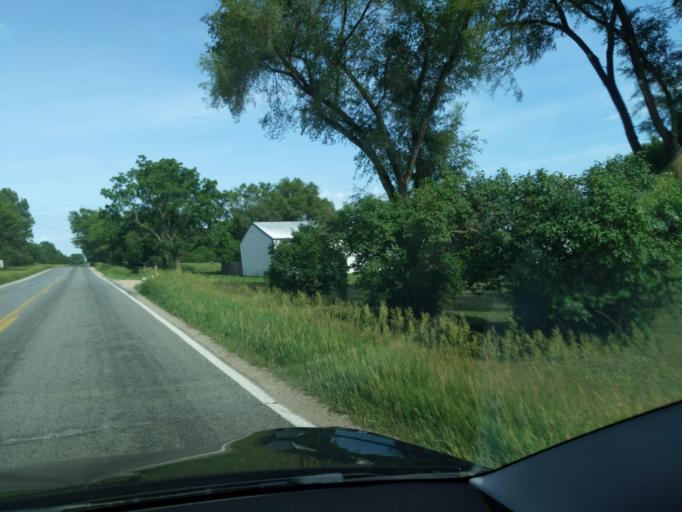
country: US
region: Michigan
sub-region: Newaygo County
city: Fremont
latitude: 43.4239
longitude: -85.9635
